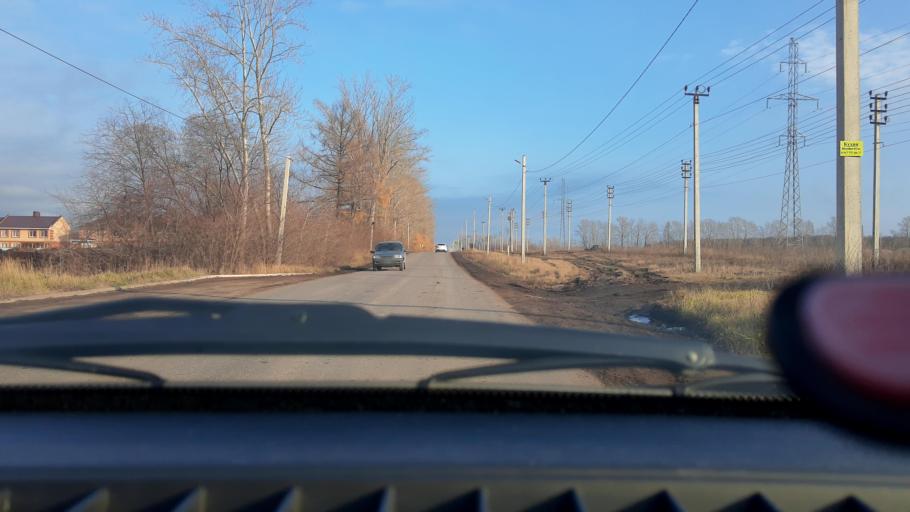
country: RU
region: Bashkortostan
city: Mikhaylovka
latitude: 54.8279
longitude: 55.8659
